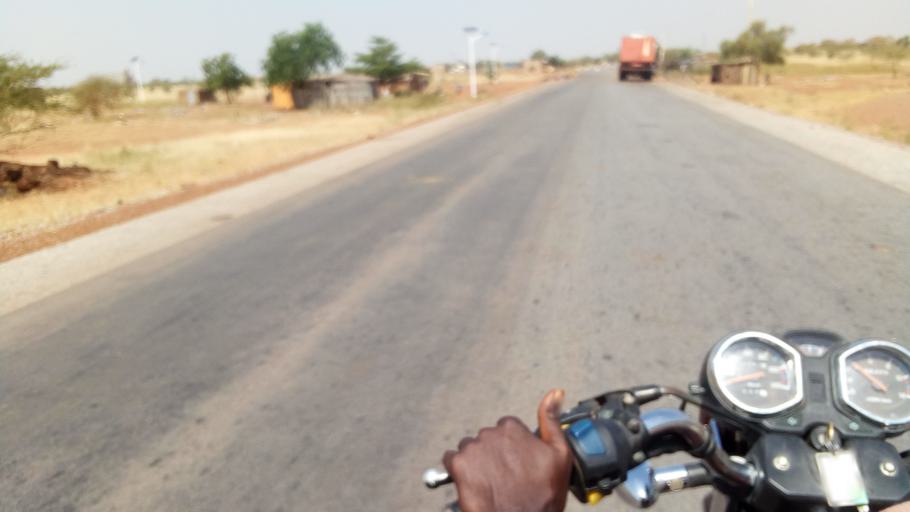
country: ML
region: Kayes
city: Kayes
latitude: 14.3962
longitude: -11.4611
